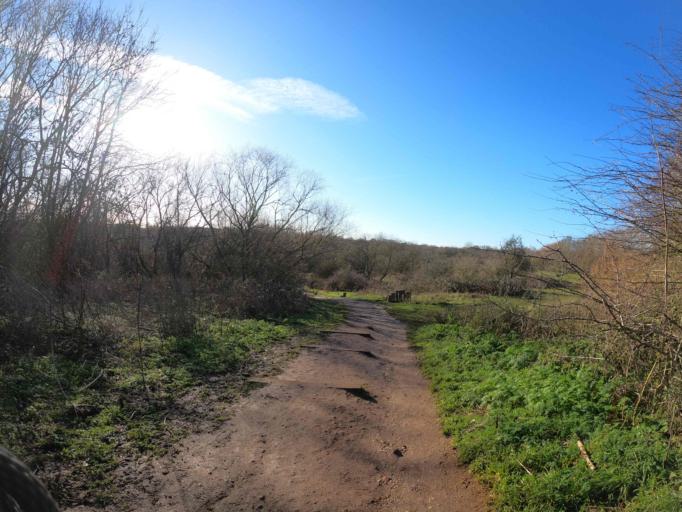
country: GB
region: England
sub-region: Greater London
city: Isleworth
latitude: 51.4984
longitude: -0.3327
